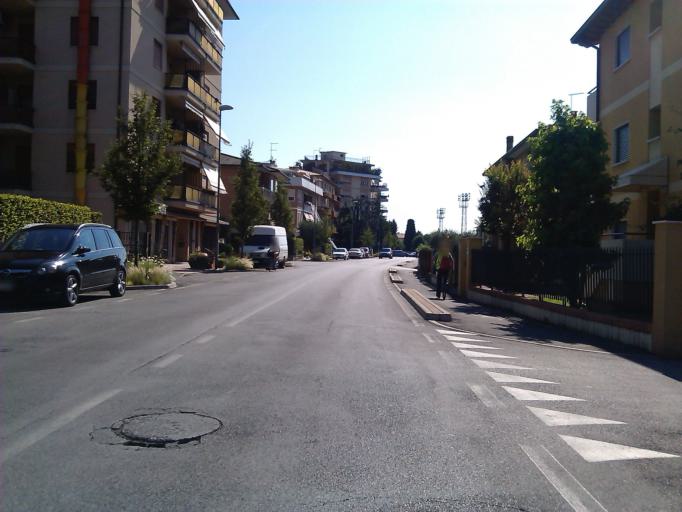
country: IT
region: Veneto
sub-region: Provincia di Vicenza
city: Bassano del Grappa
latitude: 45.7719
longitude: 11.7464
